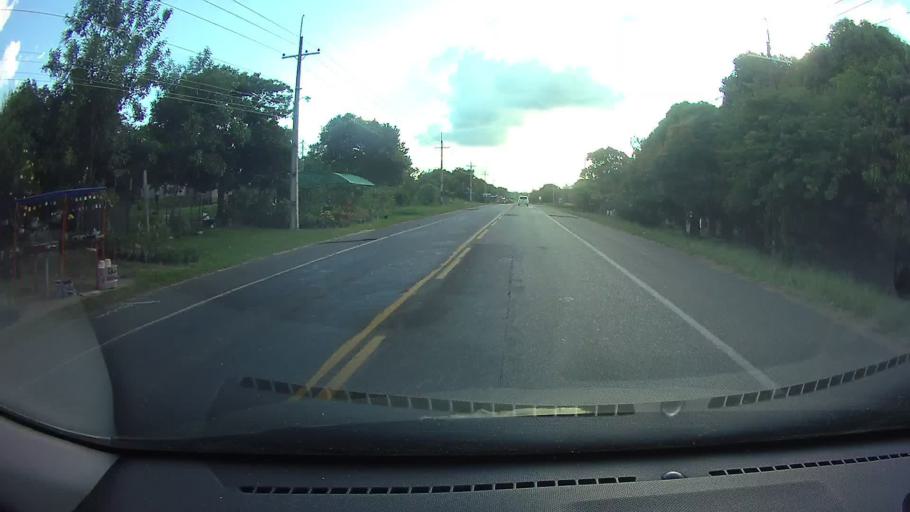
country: PY
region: Cordillera
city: Eusebio Ayala
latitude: -25.3767
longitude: -57.0304
